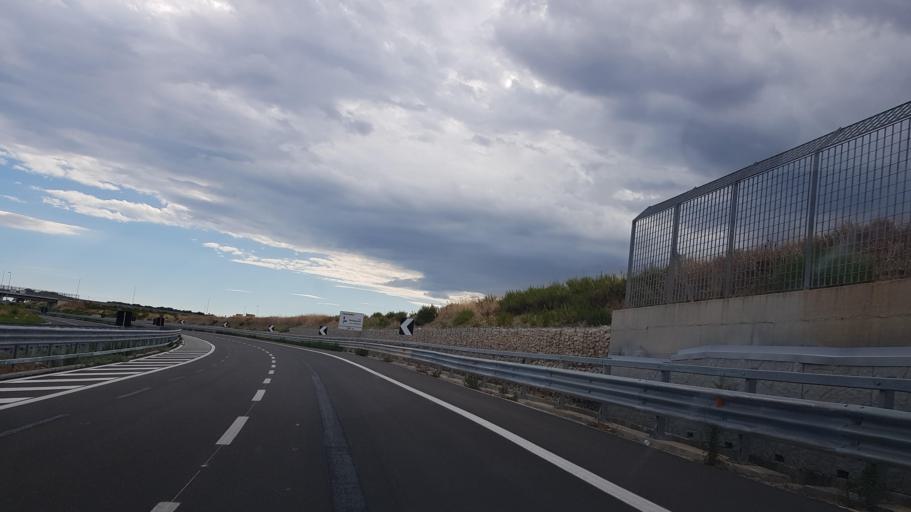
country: IT
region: Apulia
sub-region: Provincia di Taranto
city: Taranto
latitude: 40.4582
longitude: 17.2848
